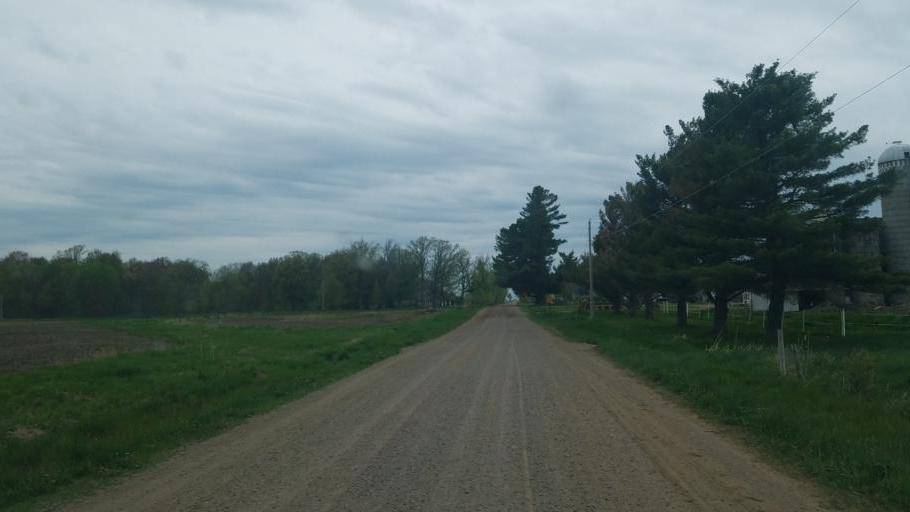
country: US
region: Wisconsin
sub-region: Clark County
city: Loyal
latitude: 44.6380
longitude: -90.4176
